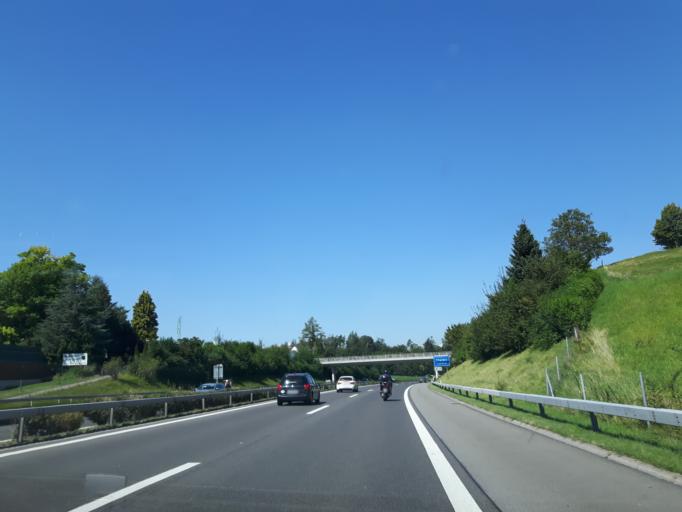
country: CH
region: Zurich
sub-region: Bezirk Horgen
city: Thalwil / Berg
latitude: 47.2905
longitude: 8.5512
